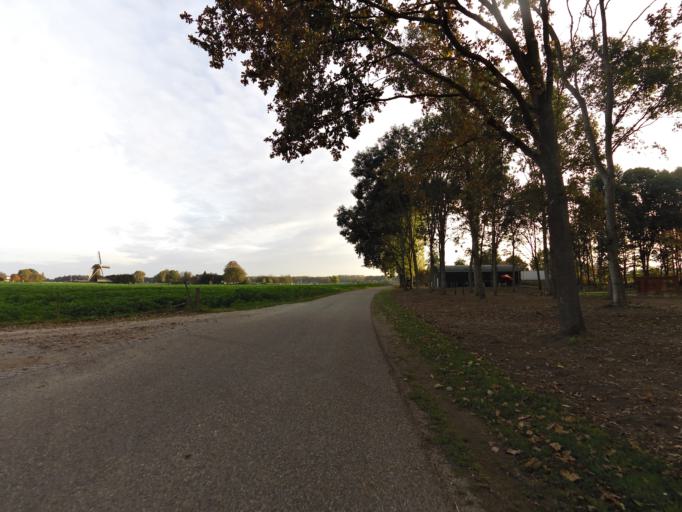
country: NL
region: Gelderland
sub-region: Gemeente Doesburg
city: Doesburg
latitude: 51.9692
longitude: 6.1791
